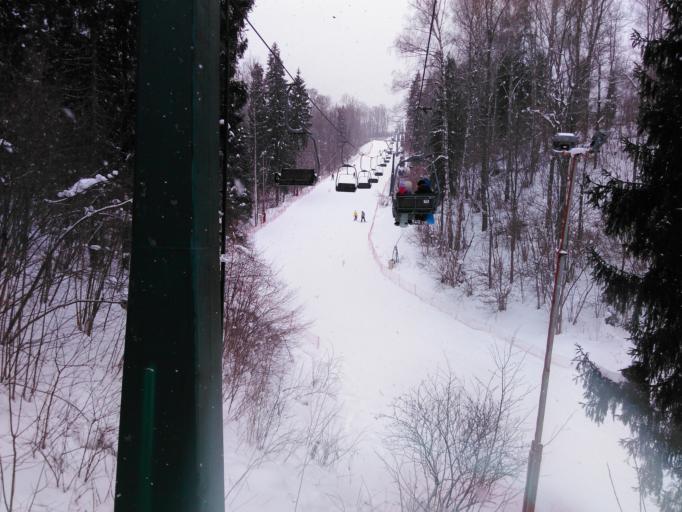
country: RU
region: Moskovskaya
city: Yakhroma
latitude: 56.2554
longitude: 37.4357
